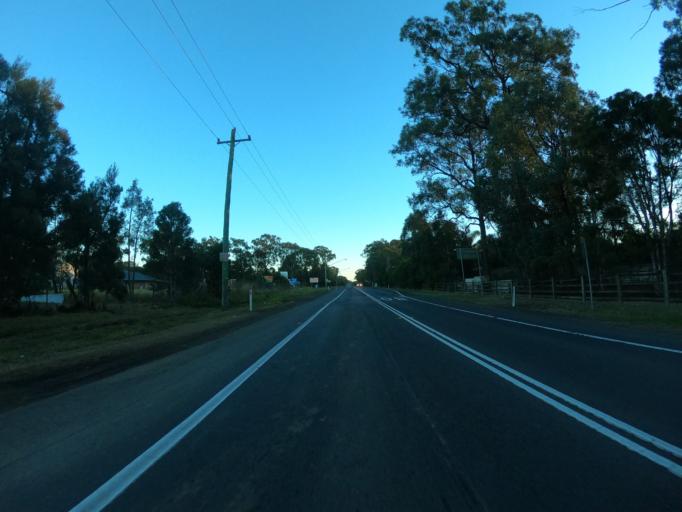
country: AU
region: New South Wales
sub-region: Hawkesbury
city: South Windsor
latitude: -33.6599
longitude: 150.7963
